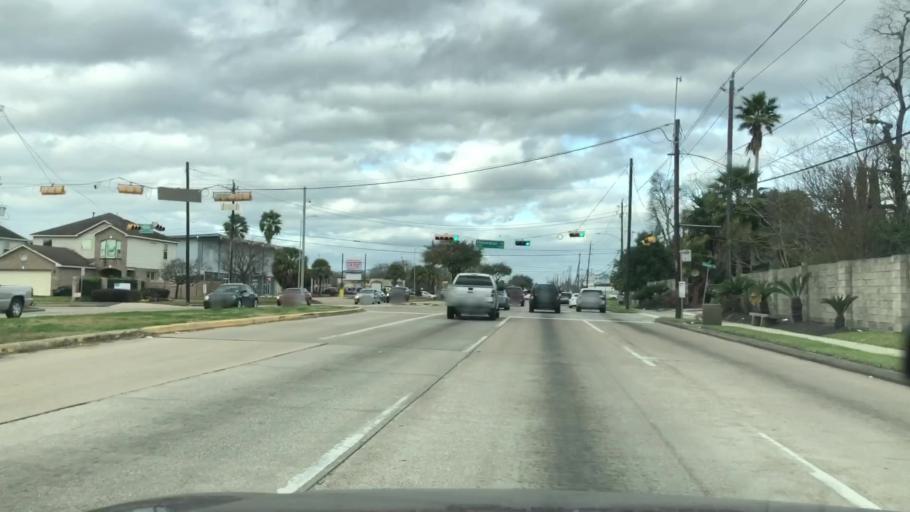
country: US
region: Texas
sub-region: Harris County
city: Bellaire
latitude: 29.6335
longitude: -95.4635
